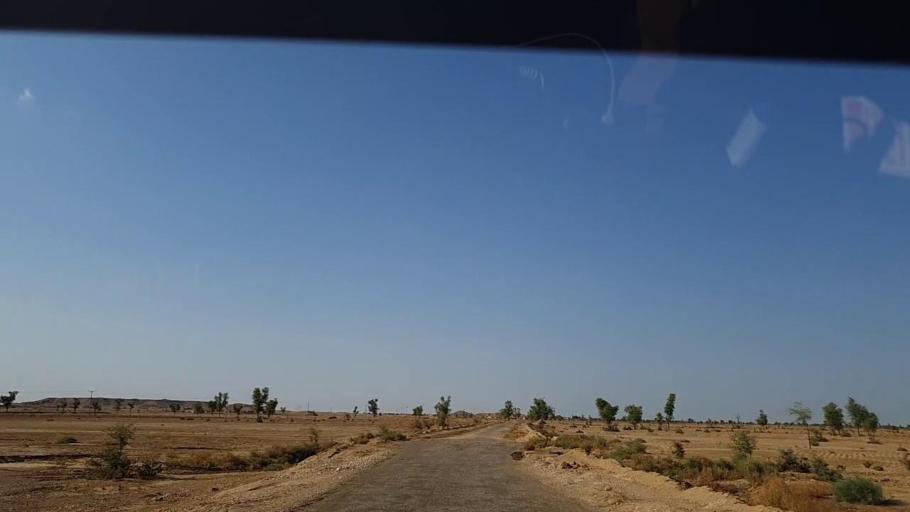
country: PK
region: Sindh
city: Johi
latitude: 26.5327
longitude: 67.5076
